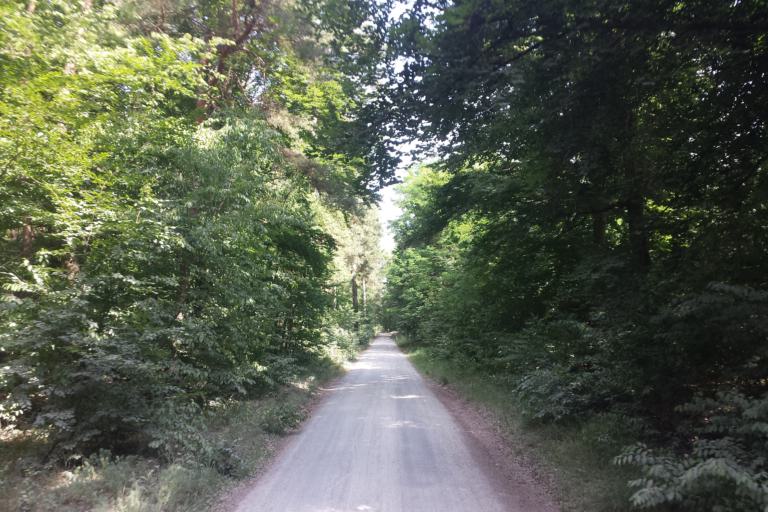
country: DE
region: Hesse
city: Lampertheim
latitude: 49.6134
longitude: 8.5101
